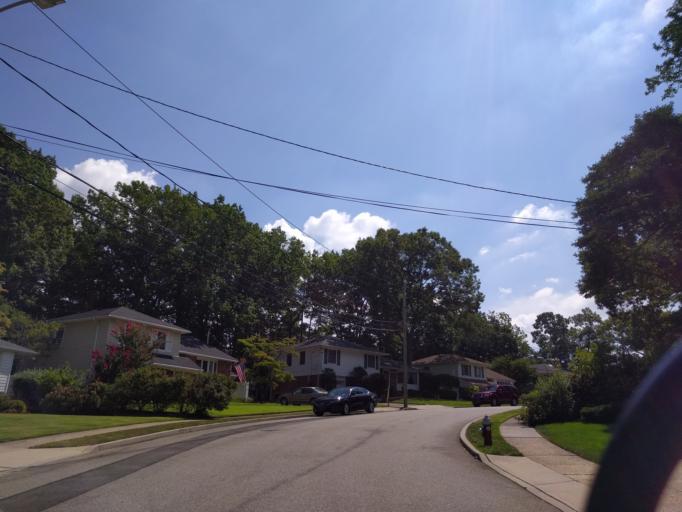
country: US
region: New York
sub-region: Nassau County
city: Oyster Bay
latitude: 40.8599
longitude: -73.5313
